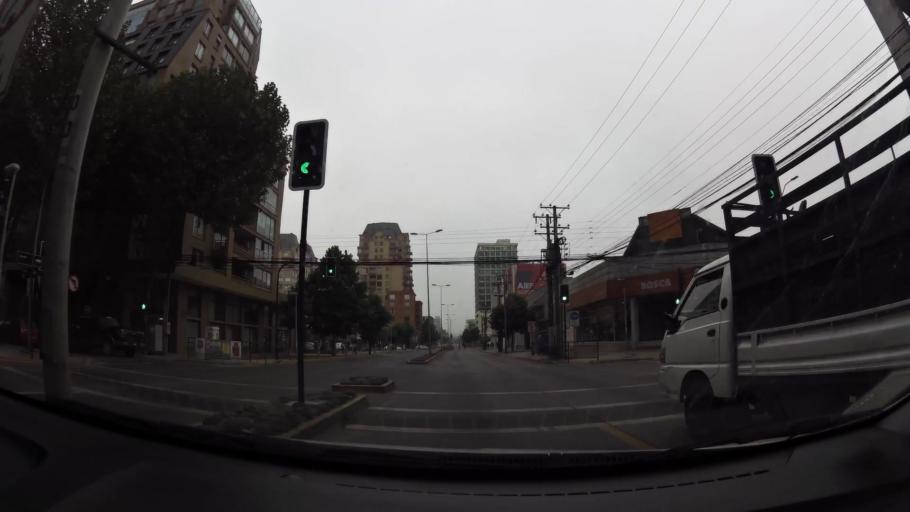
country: CL
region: Biobio
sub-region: Provincia de Concepcion
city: Concepcion
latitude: -36.8332
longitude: -73.0566
